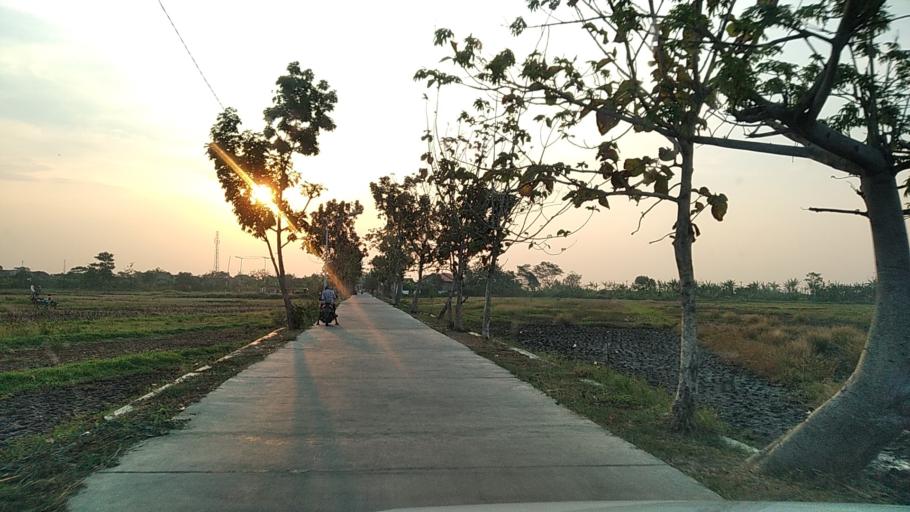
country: ID
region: Central Java
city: Semarang
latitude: -6.9589
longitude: 110.3067
